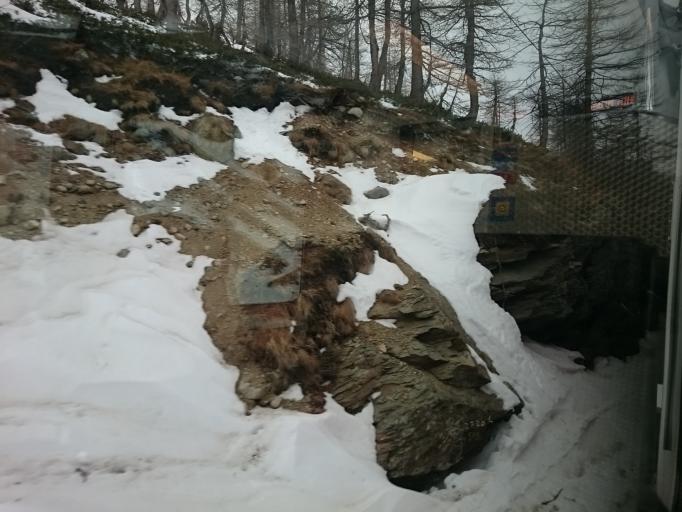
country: CH
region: Grisons
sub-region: Bernina District
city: Poschiavo
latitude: 46.3827
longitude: 10.0315
